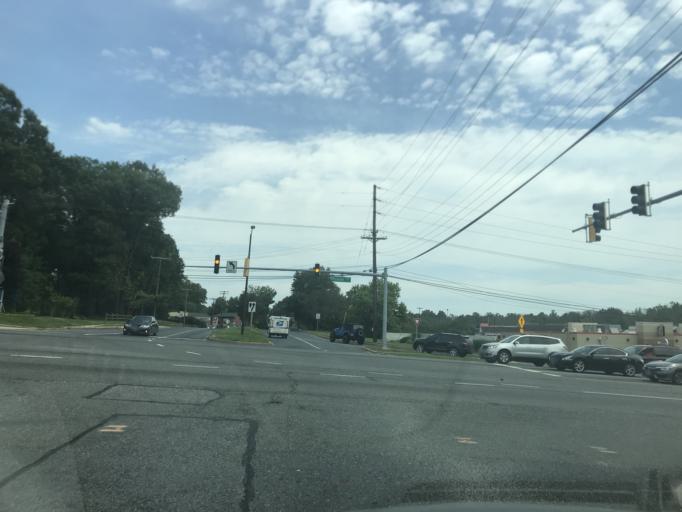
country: US
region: Maryland
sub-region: Harford County
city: Joppatowne
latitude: 39.4234
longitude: -76.3714
